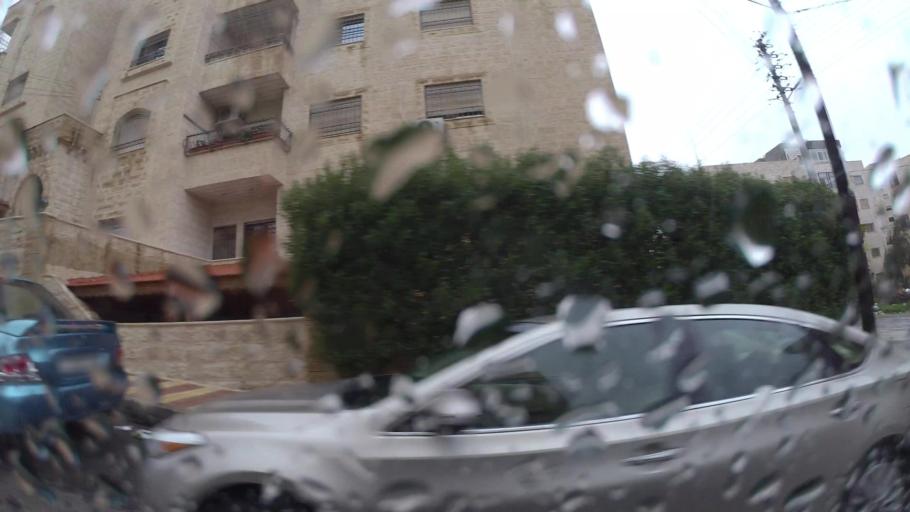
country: JO
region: Amman
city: Amman
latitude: 32.0038
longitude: 35.9307
